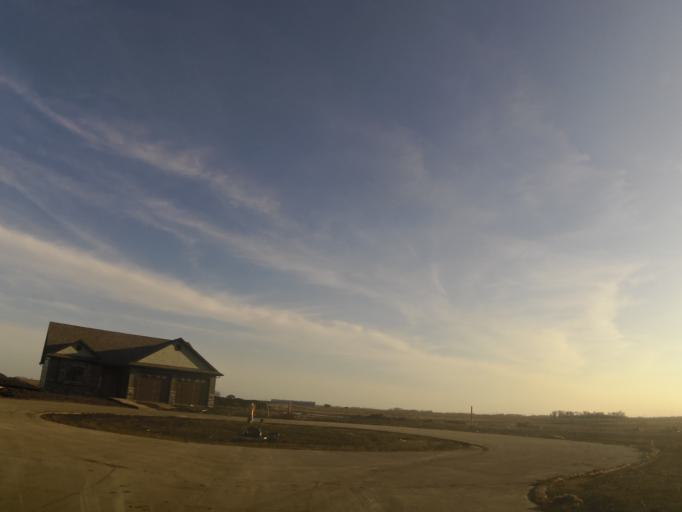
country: US
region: North Dakota
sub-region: Grand Forks County
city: Grand Forks
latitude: 47.8646
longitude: -97.0329
